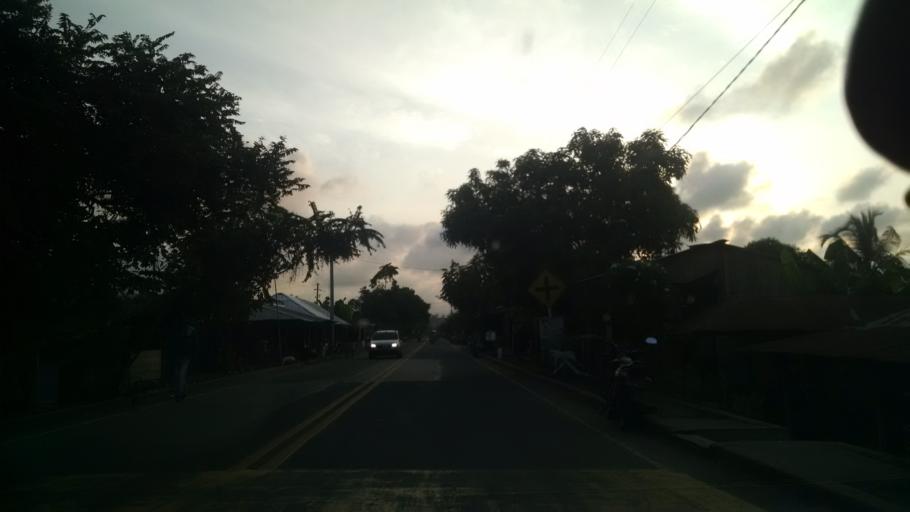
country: CO
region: Antioquia
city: San Juan de Uraba
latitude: 8.7185
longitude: -76.5980
